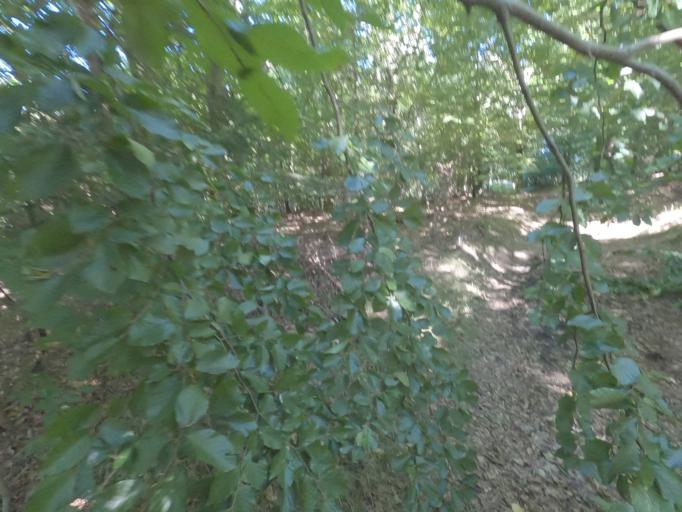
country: DE
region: Bavaria
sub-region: Lower Bavaria
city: Niederalteich
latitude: 48.8186
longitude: 13.0133
